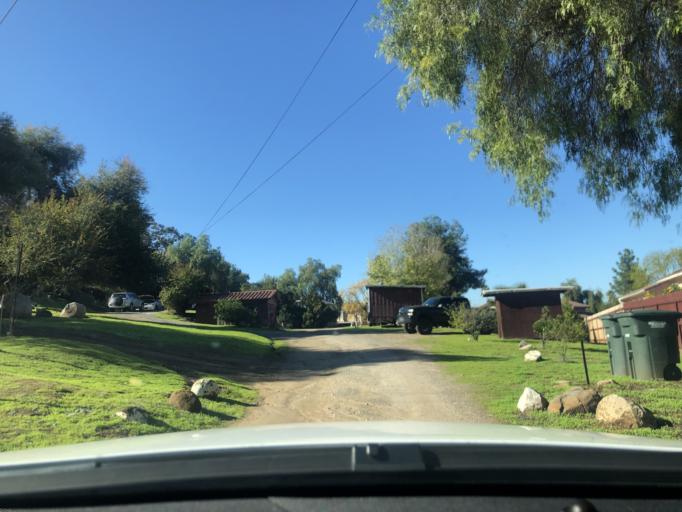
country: US
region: California
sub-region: San Diego County
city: El Cajon
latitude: 32.7793
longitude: -116.9484
